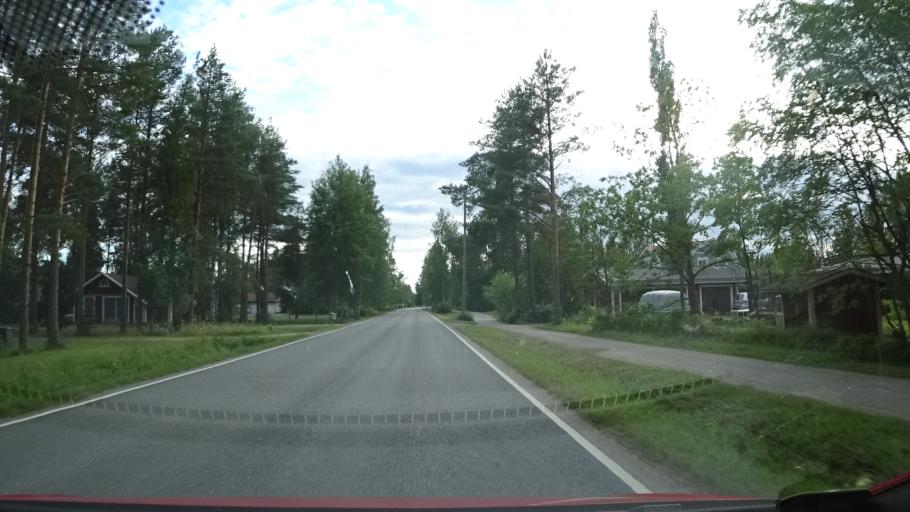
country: FI
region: Northern Ostrobothnia
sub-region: Oulu
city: Liminka
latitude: 64.8080
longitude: 25.4361
